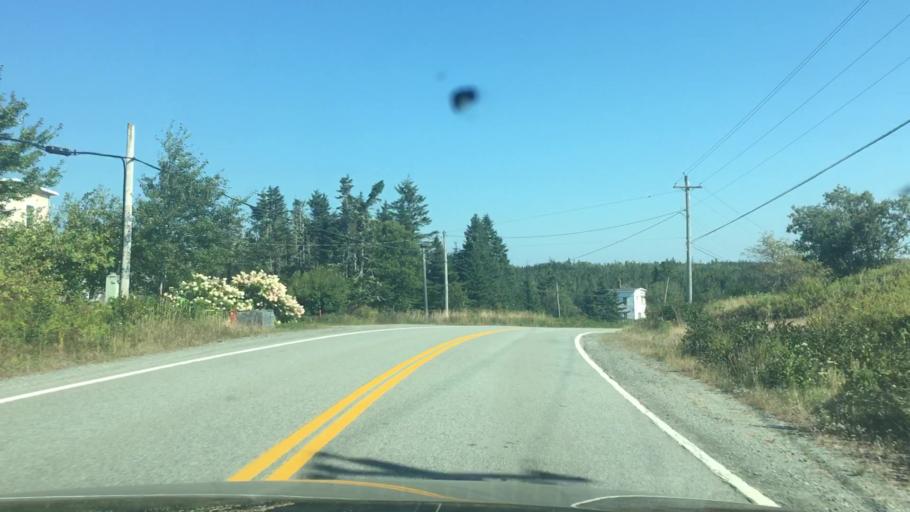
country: CA
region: Nova Scotia
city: Cole Harbour
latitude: 44.7987
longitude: -62.7163
